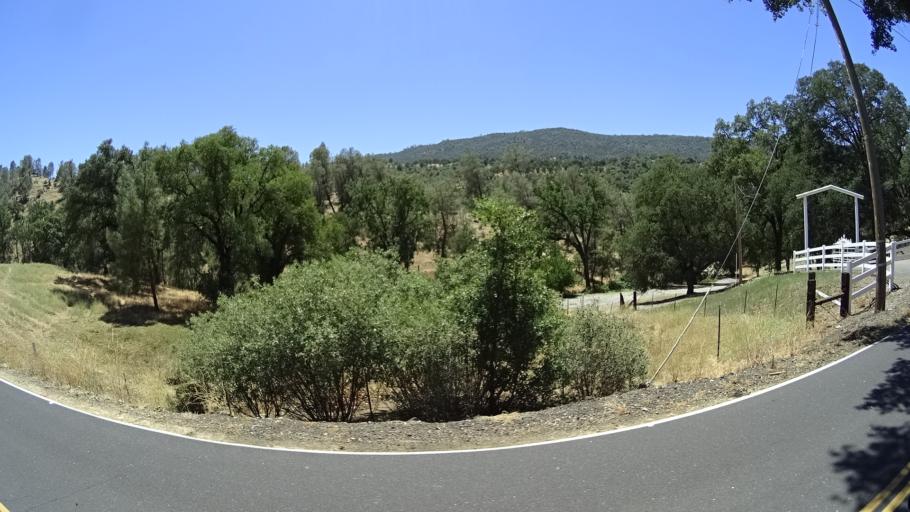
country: US
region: California
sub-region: Calaveras County
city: San Andreas
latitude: 38.1556
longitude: -120.6666
